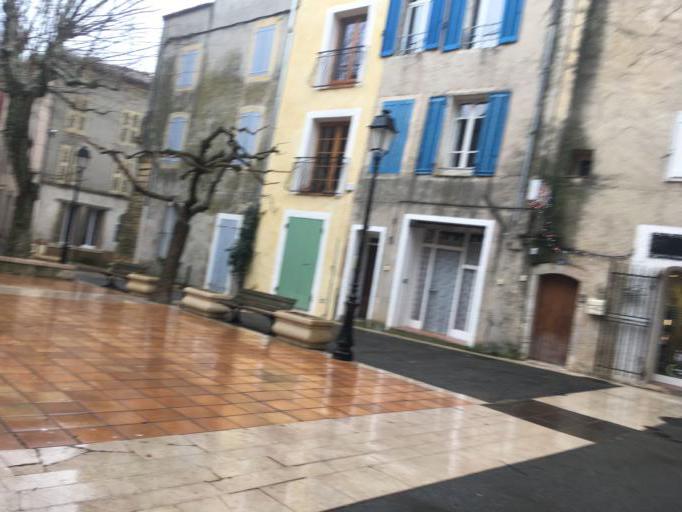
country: FR
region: Provence-Alpes-Cote d'Azur
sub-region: Departement du Var
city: Rians
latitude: 43.6067
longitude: 5.7559
